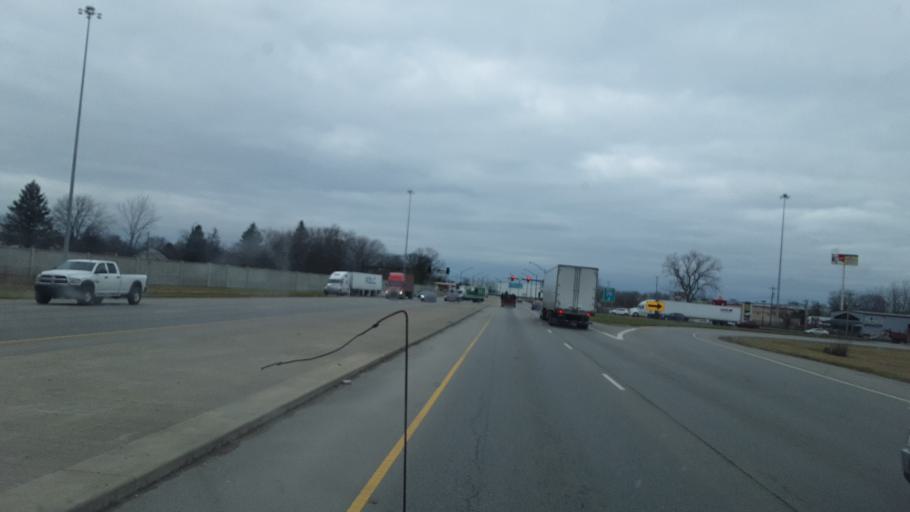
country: US
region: Ohio
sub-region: Franklin County
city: Obetz
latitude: 39.8729
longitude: -82.9330
